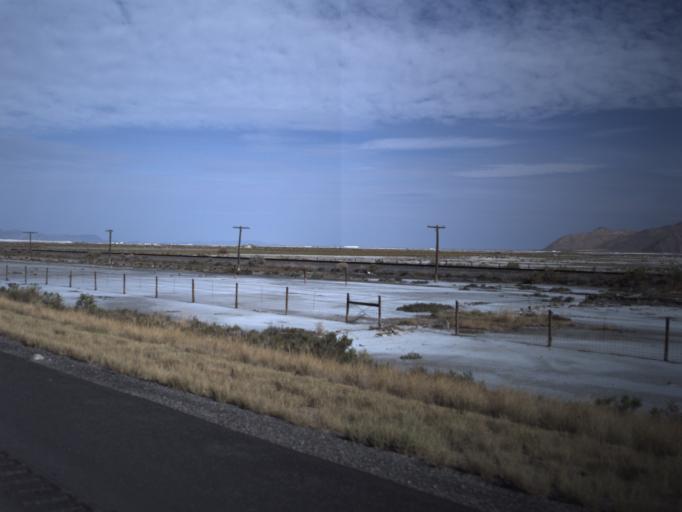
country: US
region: Utah
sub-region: Tooele County
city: Grantsville
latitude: 40.7005
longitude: -112.4868
